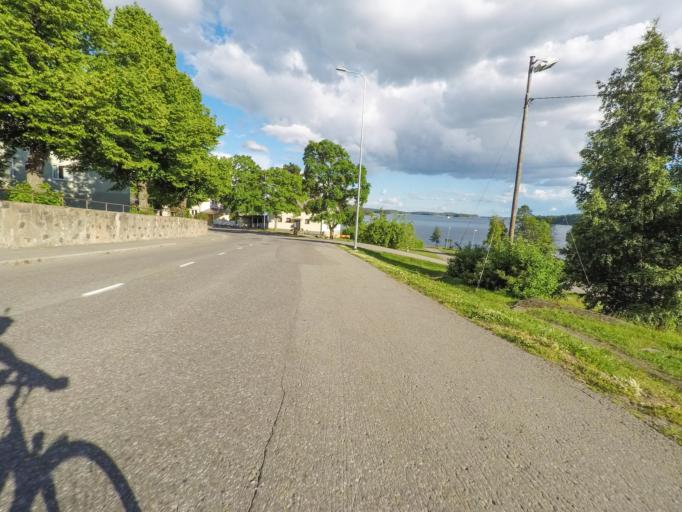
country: FI
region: Southern Savonia
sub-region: Savonlinna
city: Savonlinna
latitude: 61.8635
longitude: 28.8589
